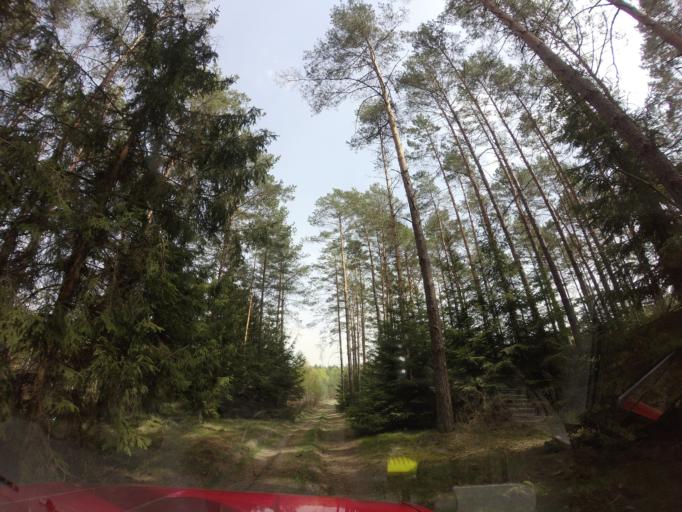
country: PL
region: West Pomeranian Voivodeship
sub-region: Powiat choszczenski
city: Drawno
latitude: 53.2773
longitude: 15.7152
